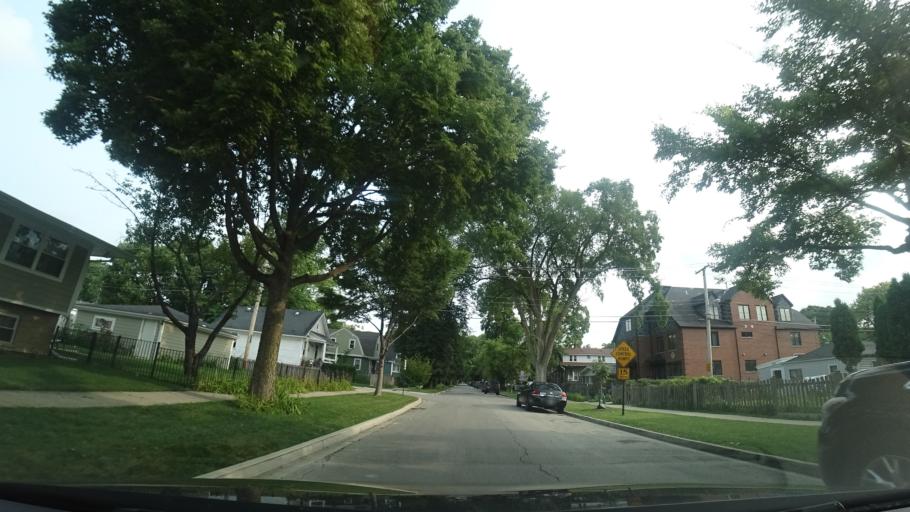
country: US
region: Illinois
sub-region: Cook County
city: Evanston
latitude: 42.0485
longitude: -87.7024
